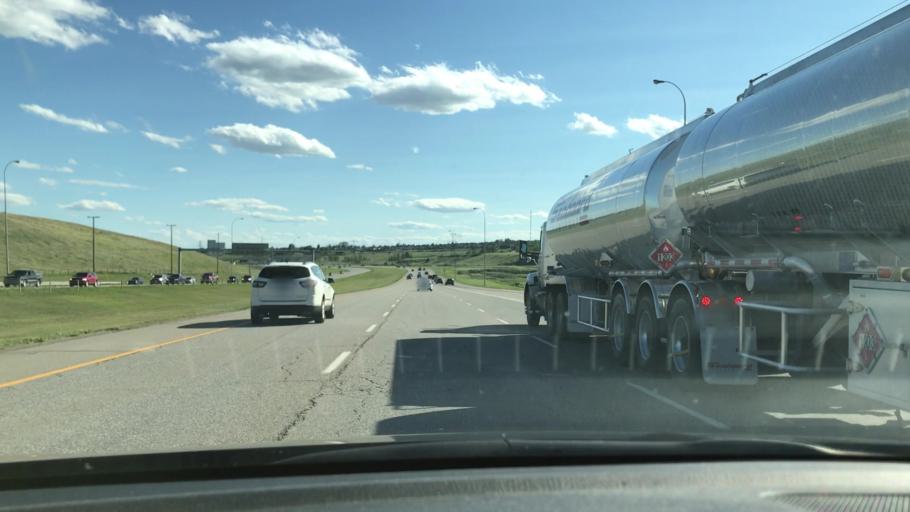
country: CA
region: Alberta
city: Calgary
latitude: 51.1379
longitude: -114.0388
